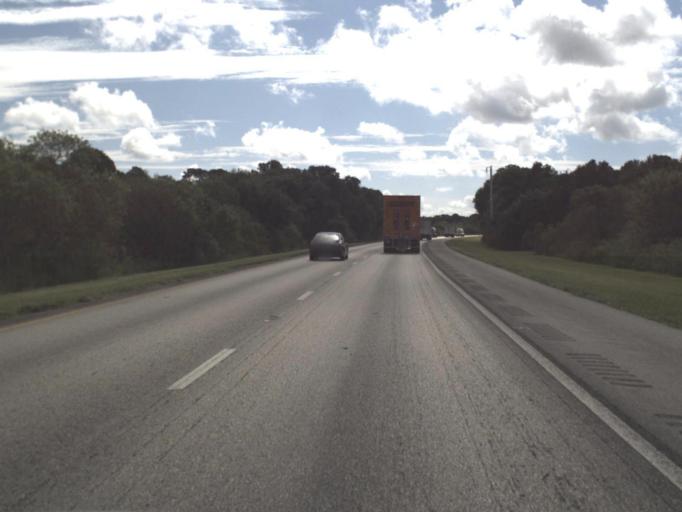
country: US
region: Florida
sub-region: Sarasota County
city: North Port
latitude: 27.0972
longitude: -82.1313
